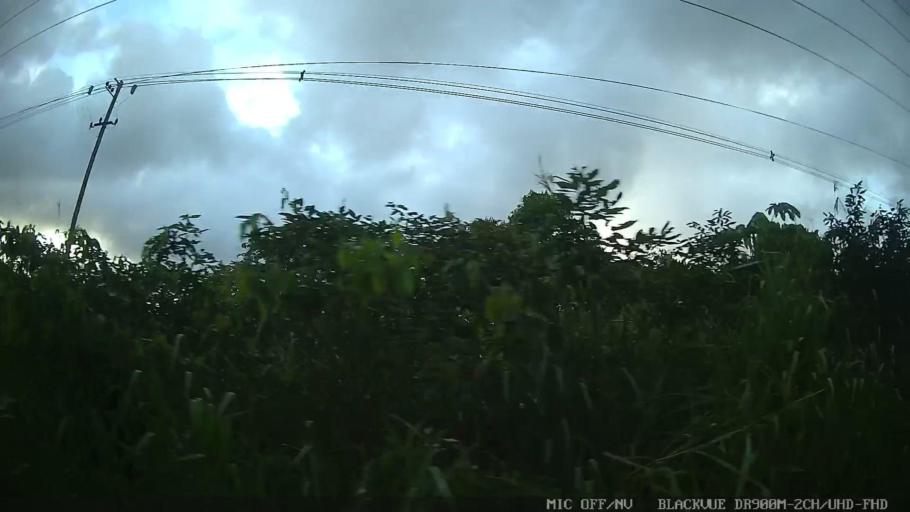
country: BR
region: Sao Paulo
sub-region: Itanhaem
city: Itanhaem
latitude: -24.0939
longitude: -46.7987
